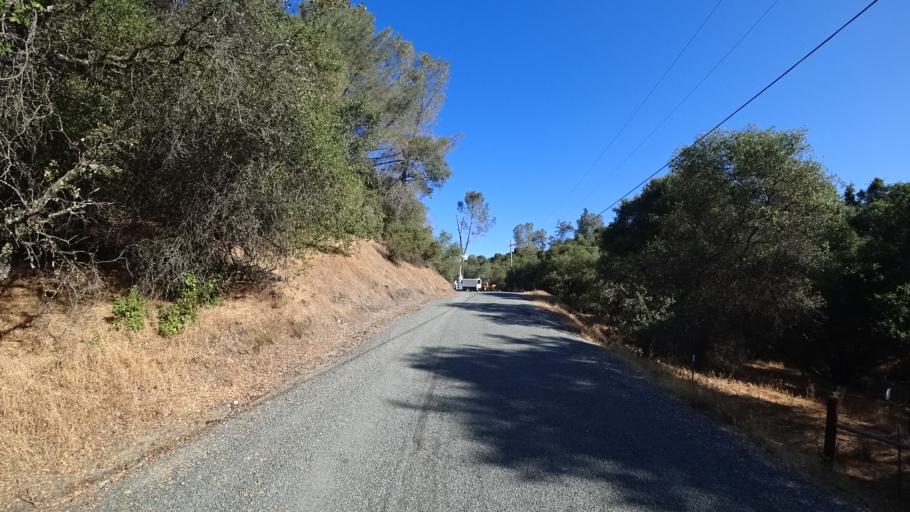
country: US
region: California
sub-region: Calaveras County
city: San Andreas
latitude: 38.2484
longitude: -120.7066
